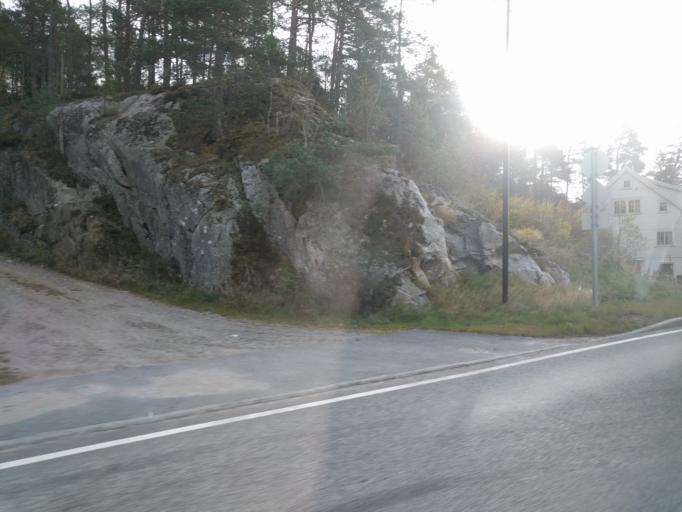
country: NO
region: Vest-Agder
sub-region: Songdalen
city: Nodeland
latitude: 58.2632
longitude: 7.8310
